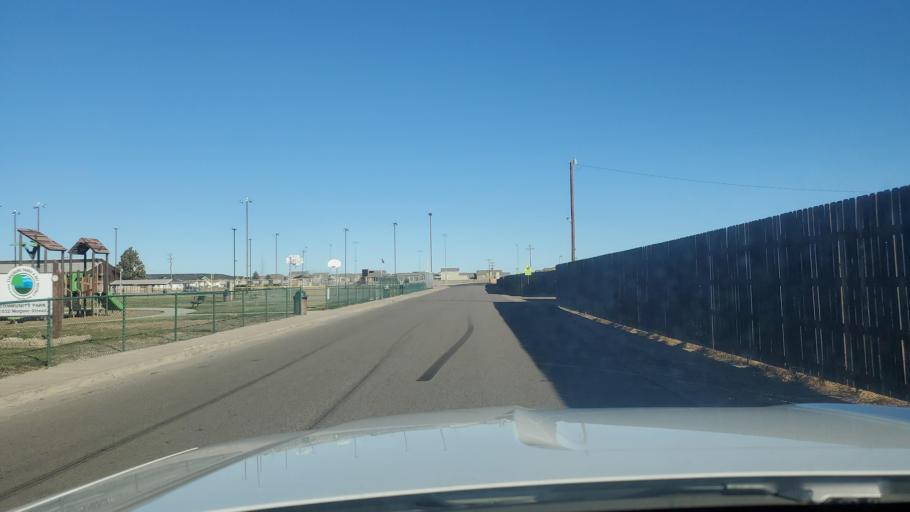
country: US
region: Colorado
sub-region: Adams County
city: Strasburg
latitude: 39.7437
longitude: -104.3264
